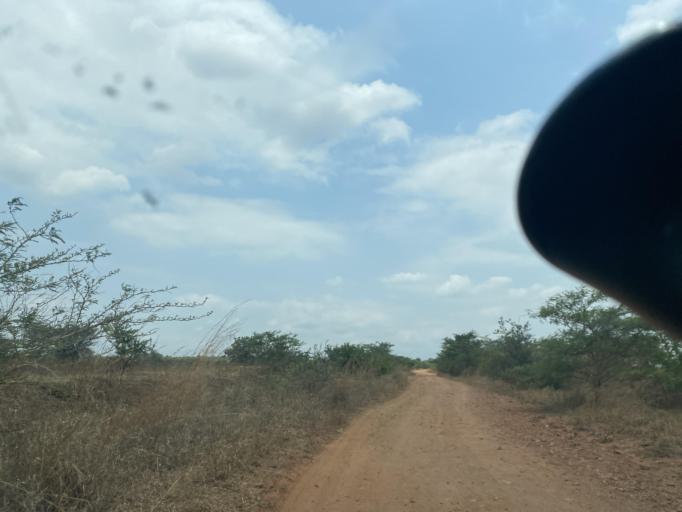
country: ZM
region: Lusaka
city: Chongwe
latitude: -15.5291
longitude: 28.8251
